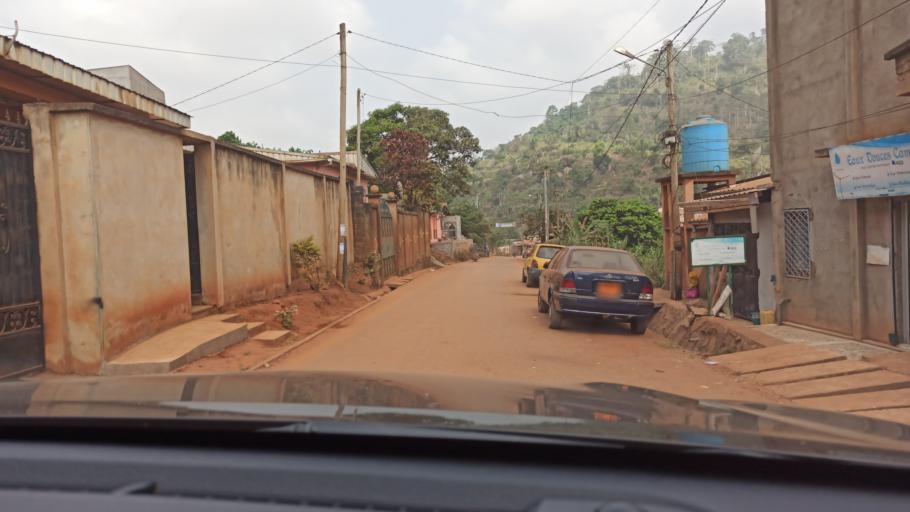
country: CM
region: Centre
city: Yaounde
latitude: 3.8789
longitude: 11.4801
